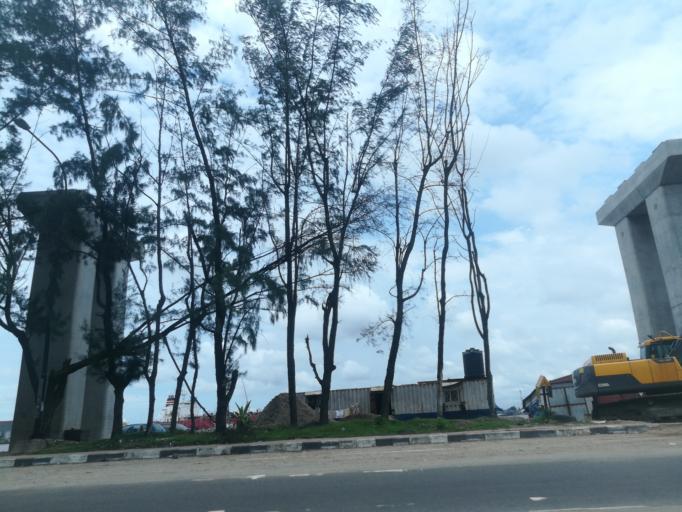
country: NG
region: Lagos
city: Lagos
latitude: 6.4576
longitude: 3.3801
